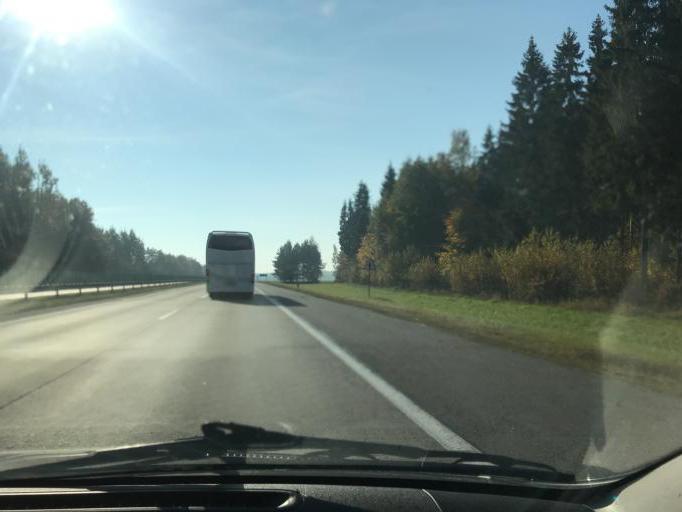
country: BY
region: Minsk
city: Samakhvalavichy
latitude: 53.5583
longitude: 27.4740
